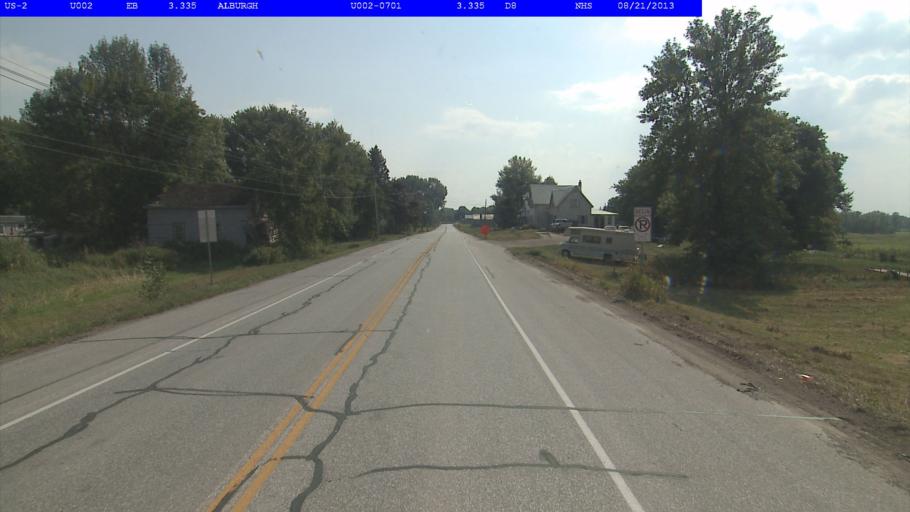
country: US
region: New York
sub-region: Clinton County
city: Rouses Point
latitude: 44.9858
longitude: -73.2965
